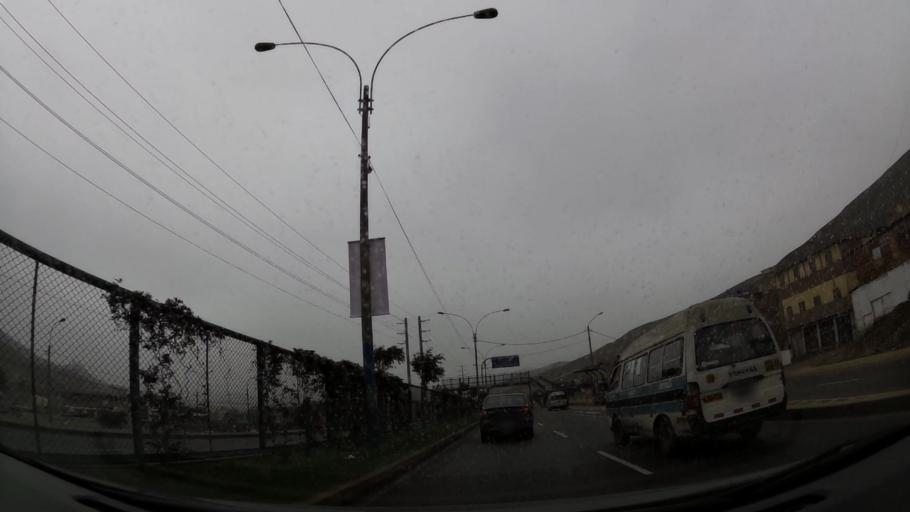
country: PE
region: Lima
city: Ventanilla
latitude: -11.8936
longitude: -77.1264
